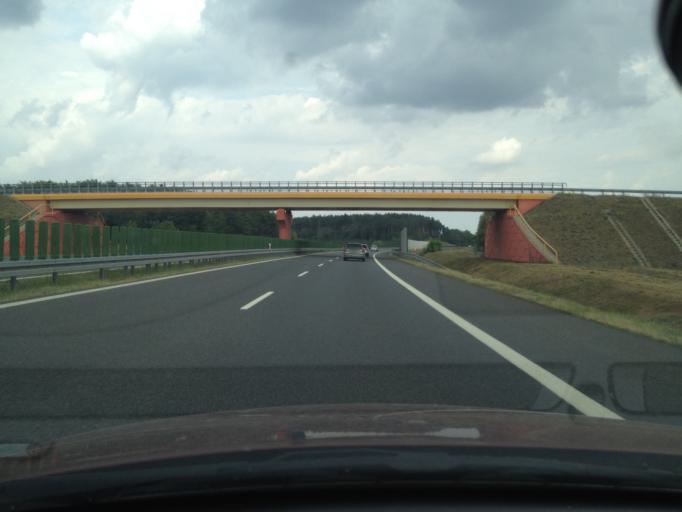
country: PL
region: West Pomeranian Voivodeship
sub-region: Powiat mysliborski
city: Mysliborz
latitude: 52.9935
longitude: 14.8638
